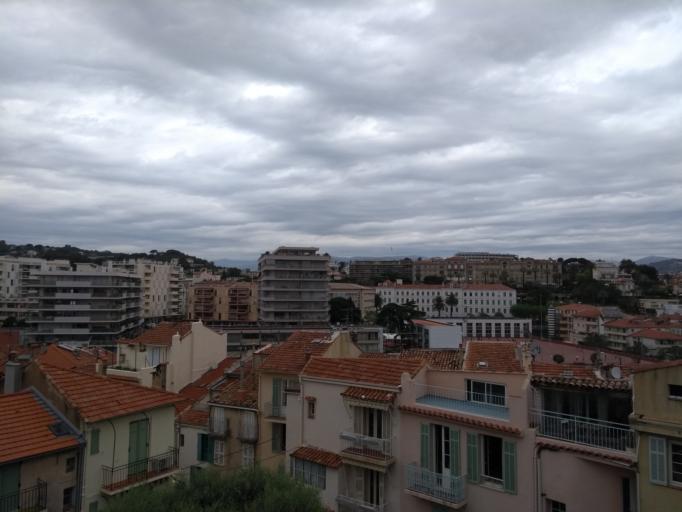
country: FR
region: Provence-Alpes-Cote d'Azur
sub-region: Departement des Alpes-Maritimes
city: Cannes
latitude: 43.5510
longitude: 7.0102
